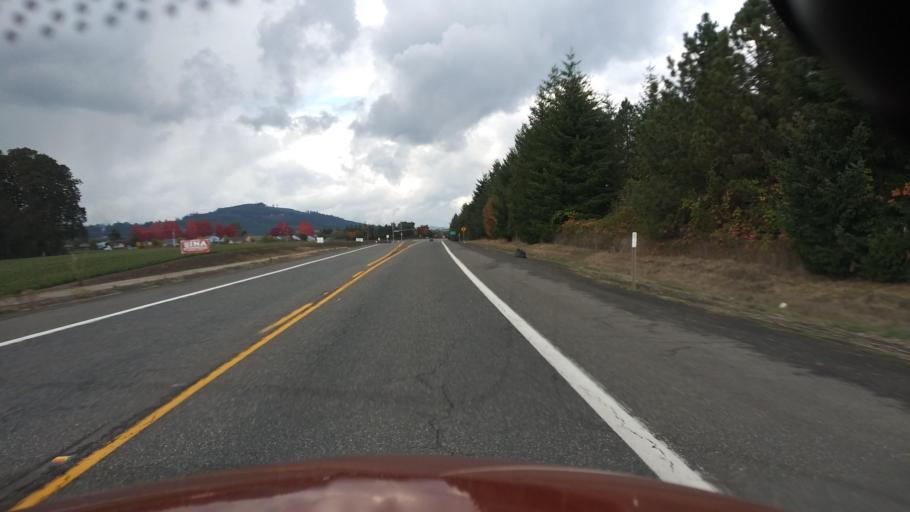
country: US
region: Oregon
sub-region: Washington County
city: Forest Grove
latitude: 45.5328
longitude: -123.1024
